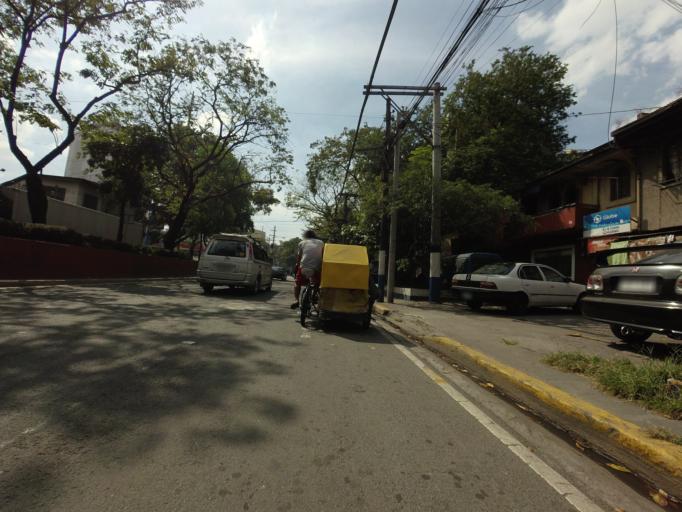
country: PH
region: Metro Manila
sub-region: City of Manila
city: Quiapo
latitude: 14.5740
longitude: 120.9944
